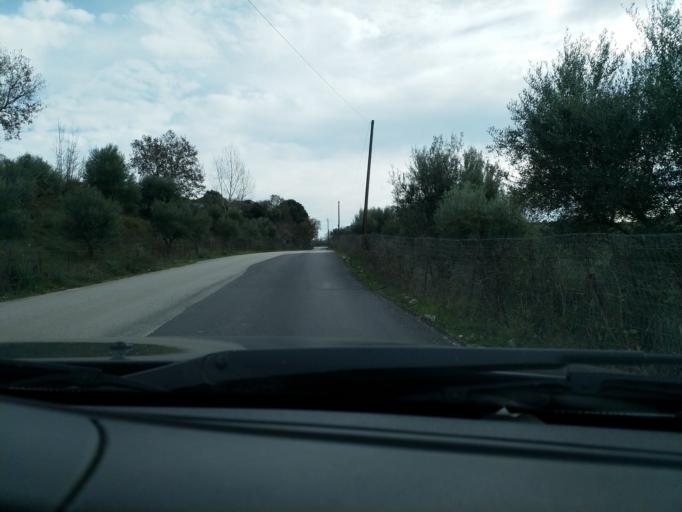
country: GR
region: Epirus
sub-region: Nomos Prevezis
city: Filippiada
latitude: 39.2223
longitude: 20.8486
